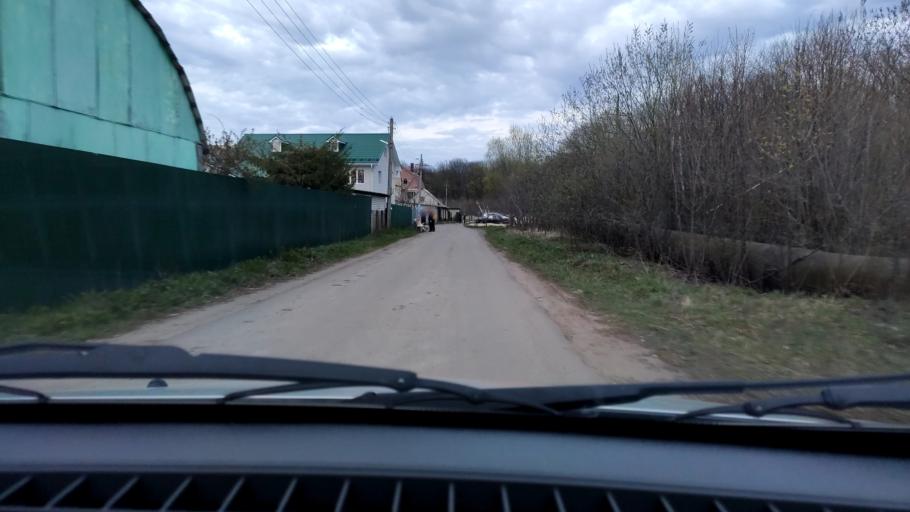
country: RU
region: Voronezj
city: Podgornoye
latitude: 51.7954
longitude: 39.2185
